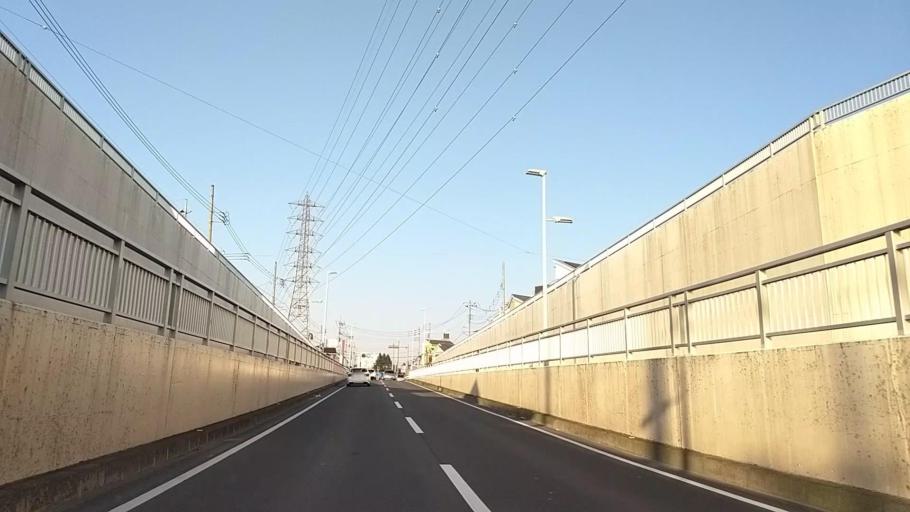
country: JP
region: Saitama
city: Tokorozawa
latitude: 35.7974
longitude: 139.4458
